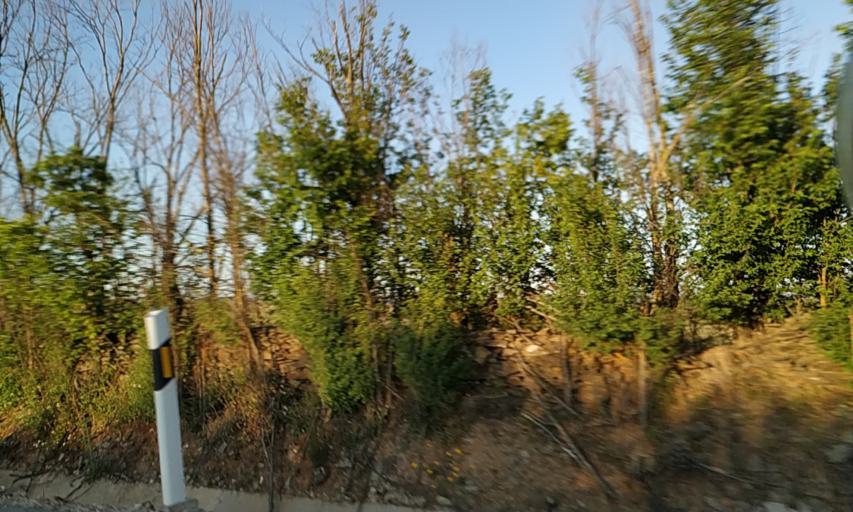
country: ES
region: Extremadura
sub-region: Provincia de Caceres
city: Valencia de Alcantara
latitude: 39.4344
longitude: -7.2234
